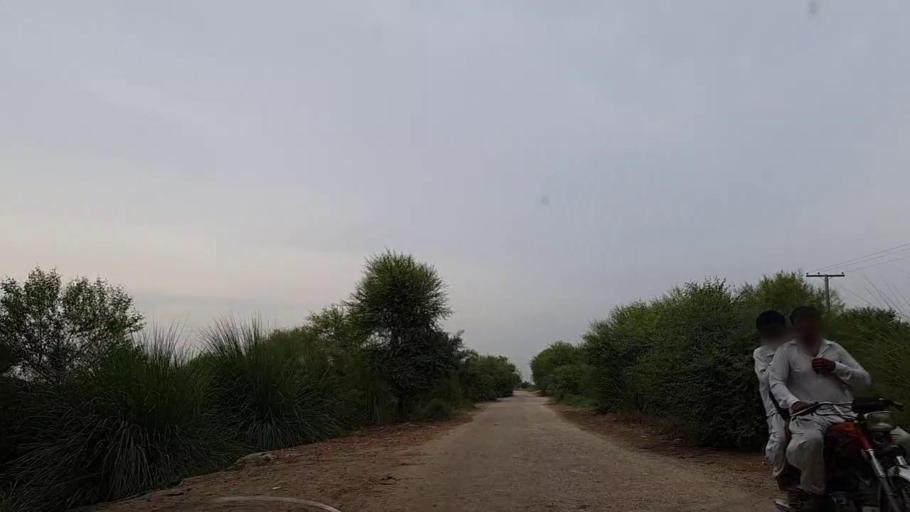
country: PK
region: Sindh
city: Mirpur Mathelo
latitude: 27.8510
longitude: 69.6300
